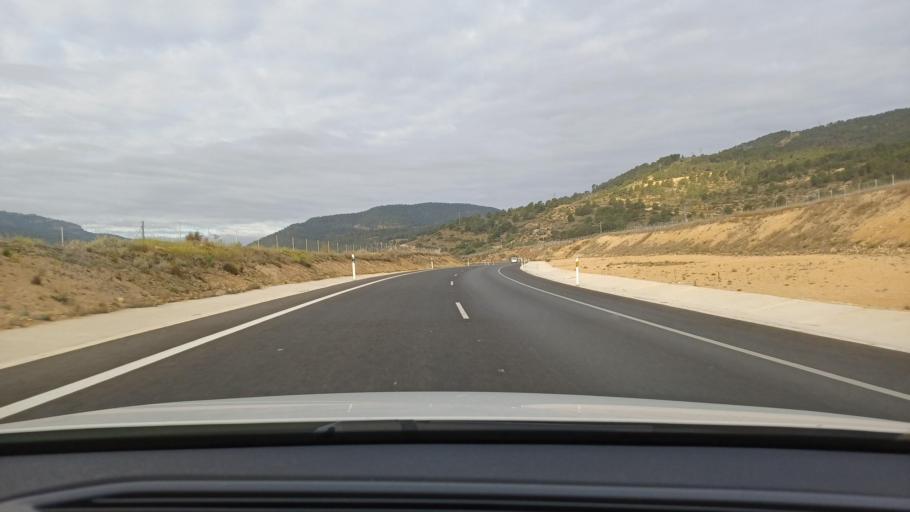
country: ES
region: Valencia
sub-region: Provincia de Valencia
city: La Font de la Figuera
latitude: 38.8302
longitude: -0.8847
